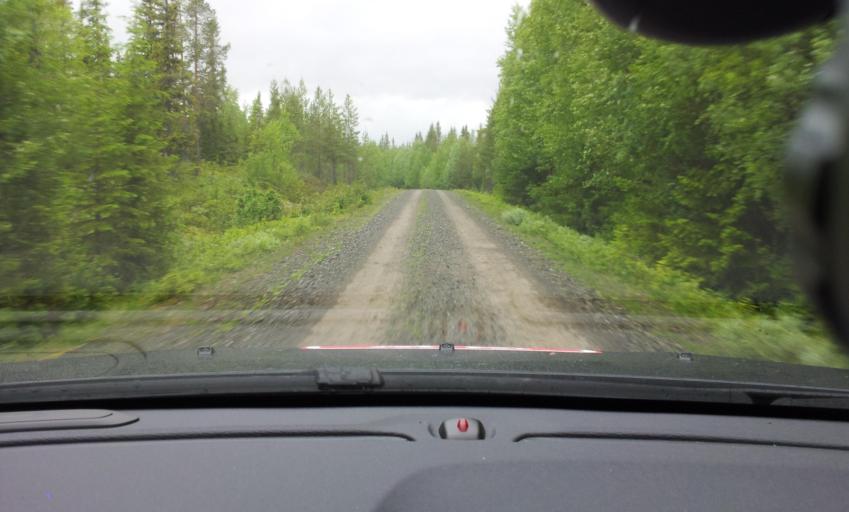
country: SE
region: Jaemtland
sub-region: Are Kommun
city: Are
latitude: 63.1886
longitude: 13.2428
